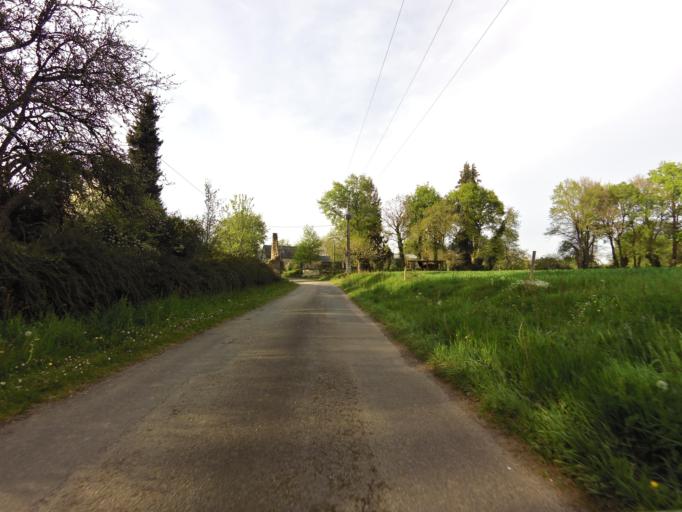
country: FR
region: Brittany
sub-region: Departement du Morbihan
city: Pluherlin
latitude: 47.7184
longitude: -2.3697
